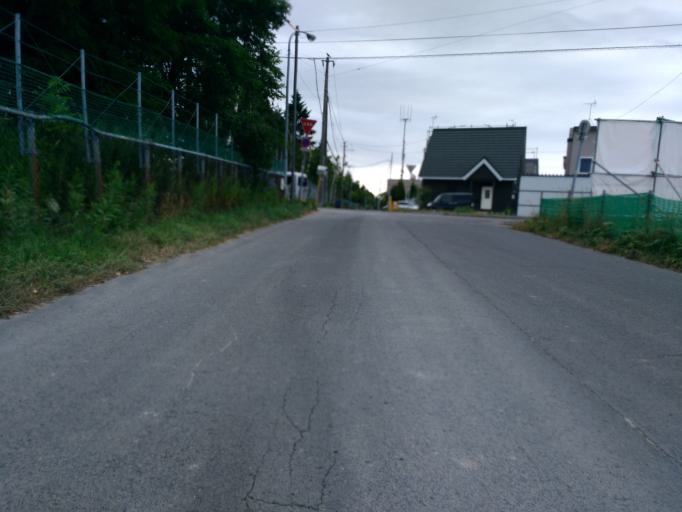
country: JP
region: Hokkaido
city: Ebetsu
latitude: 43.0817
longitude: 141.5271
